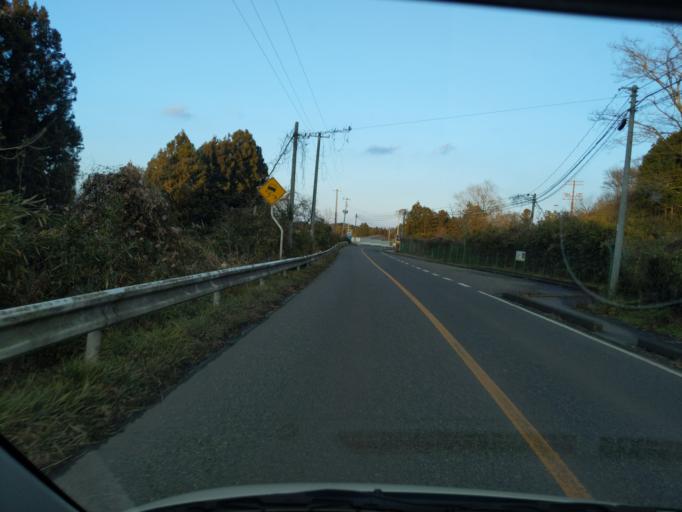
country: JP
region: Miyagi
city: Wakuya
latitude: 38.6940
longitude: 141.1478
